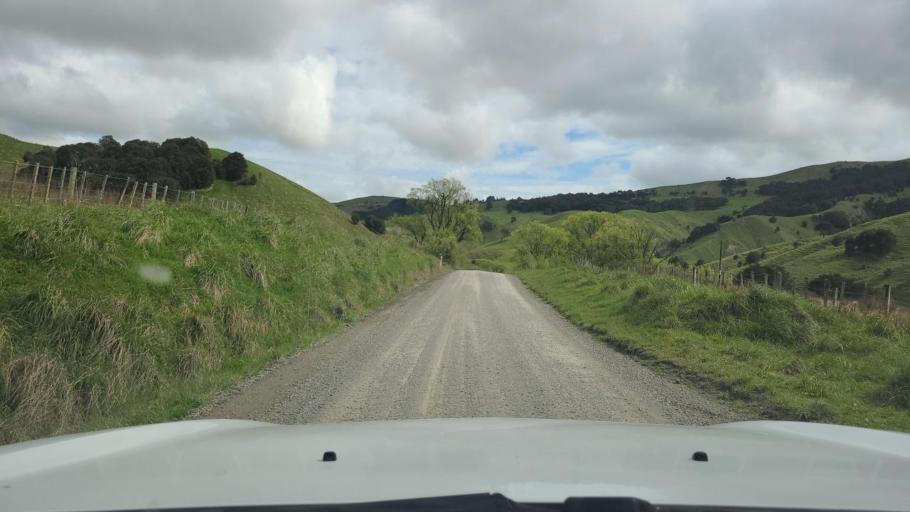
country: NZ
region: Wellington
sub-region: South Wairarapa District
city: Waipawa
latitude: -41.2917
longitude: 175.6422
